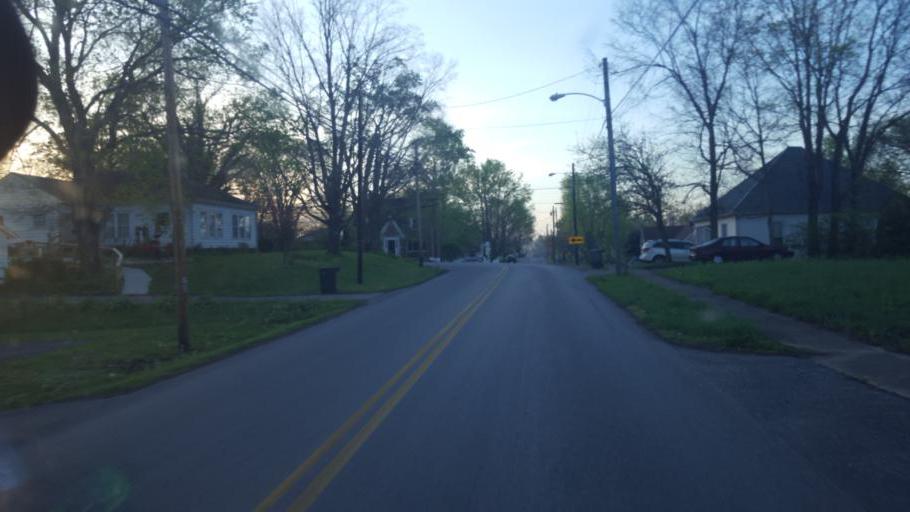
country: US
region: Kentucky
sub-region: Hart County
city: Munfordville
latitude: 37.2712
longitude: -85.8940
